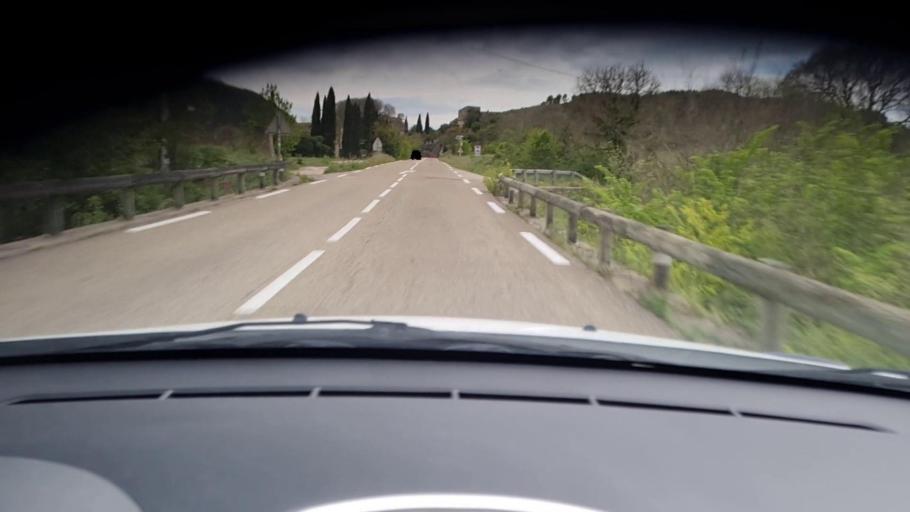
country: FR
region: Languedoc-Roussillon
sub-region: Departement du Gard
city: Blauzac
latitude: 43.9449
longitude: 4.3782
